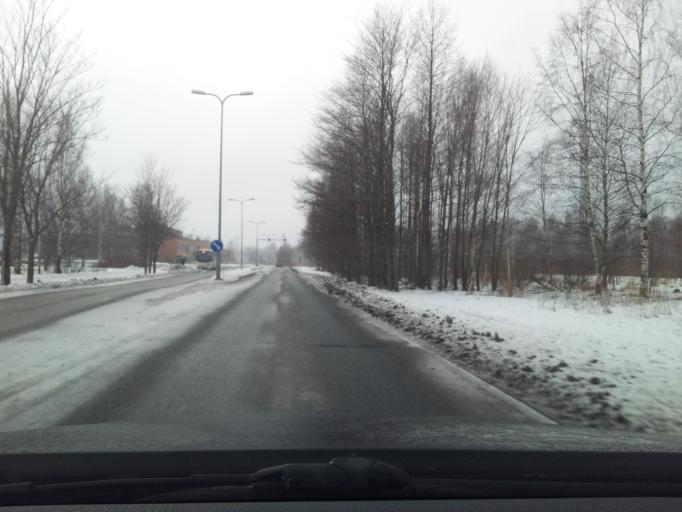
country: FI
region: Uusimaa
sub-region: Helsinki
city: Koukkuniemi
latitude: 60.1839
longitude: 24.7707
